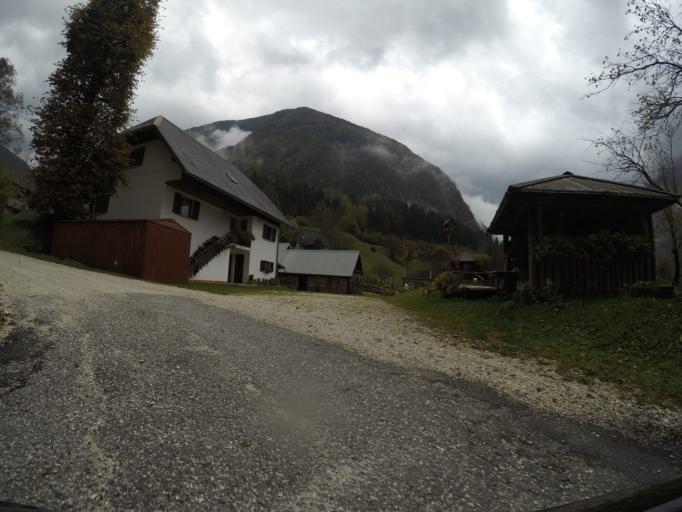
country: SI
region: Bovec
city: Bovec
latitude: 46.3374
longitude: 13.6465
